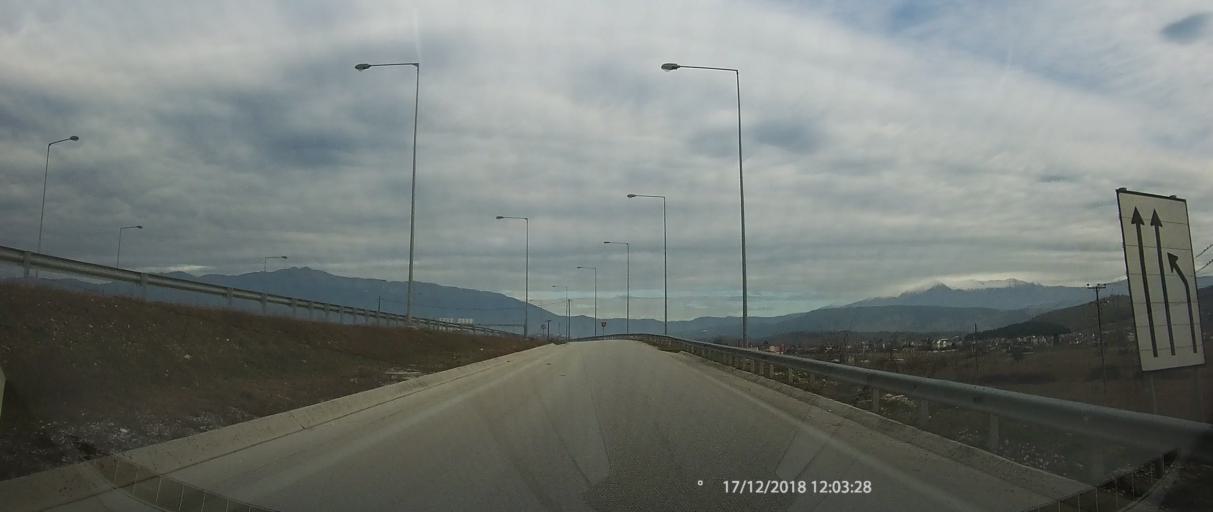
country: GR
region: Epirus
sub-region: Nomos Ioanninon
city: Pedini
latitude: 39.5967
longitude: 20.8639
